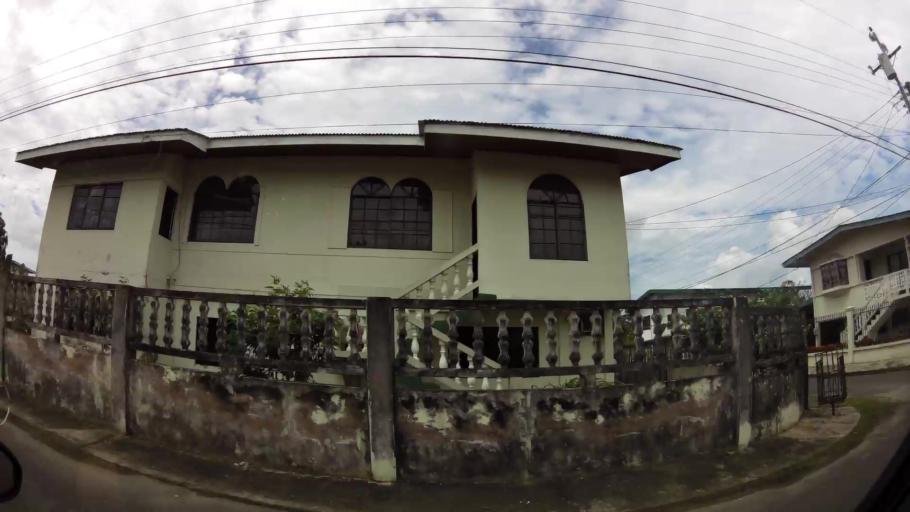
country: TT
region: Couva-Tabaquite-Talparo
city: Couva
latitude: 10.4017
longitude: -61.4684
